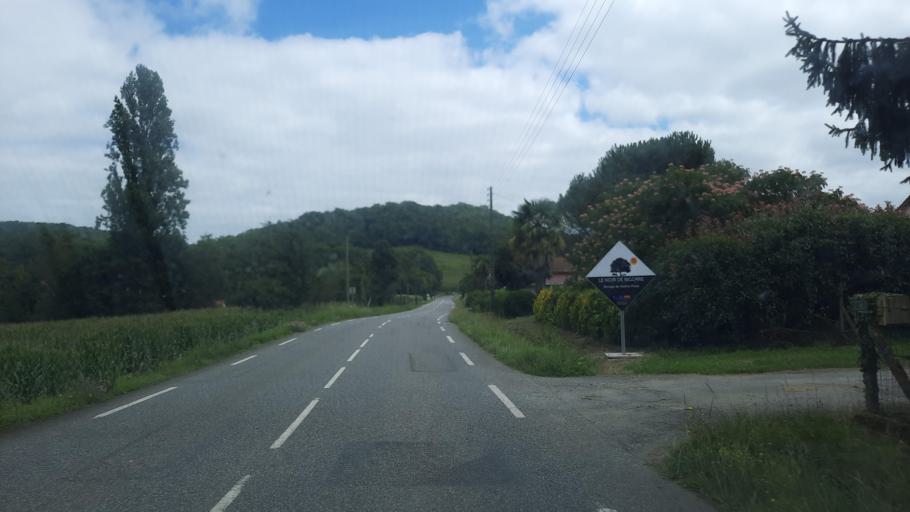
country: FR
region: Midi-Pyrenees
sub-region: Departement des Hautes-Pyrenees
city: Trie-sur-Baise
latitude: 43.3053
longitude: 0.2659
